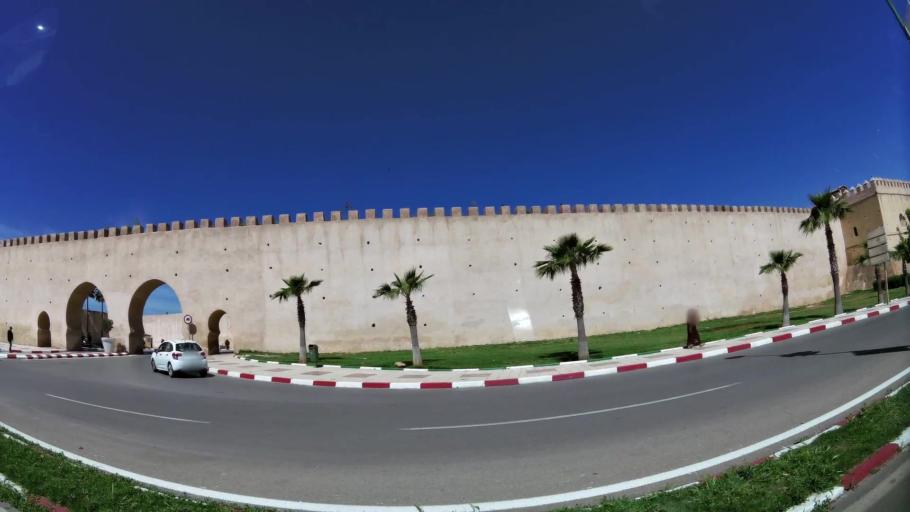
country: MA
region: Meknes-Tafilalet
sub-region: Meknes
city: Meknes
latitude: 33.8867
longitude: -5.5528
